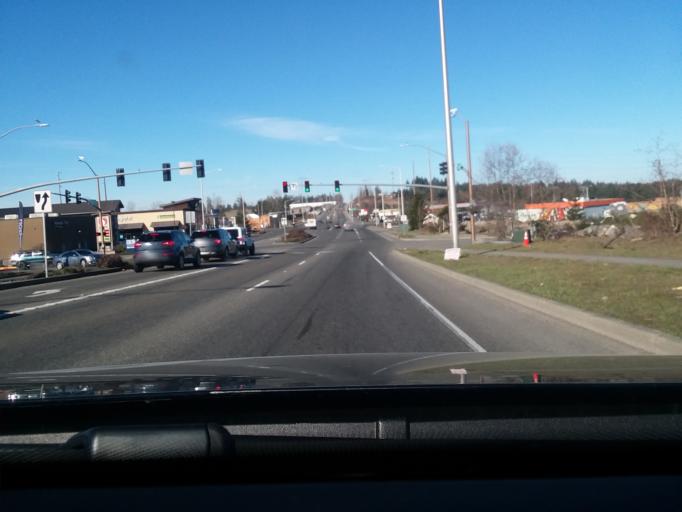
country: US
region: Washington
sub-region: Pierce County
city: Frederickson
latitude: 47.0965
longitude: -122.3536
